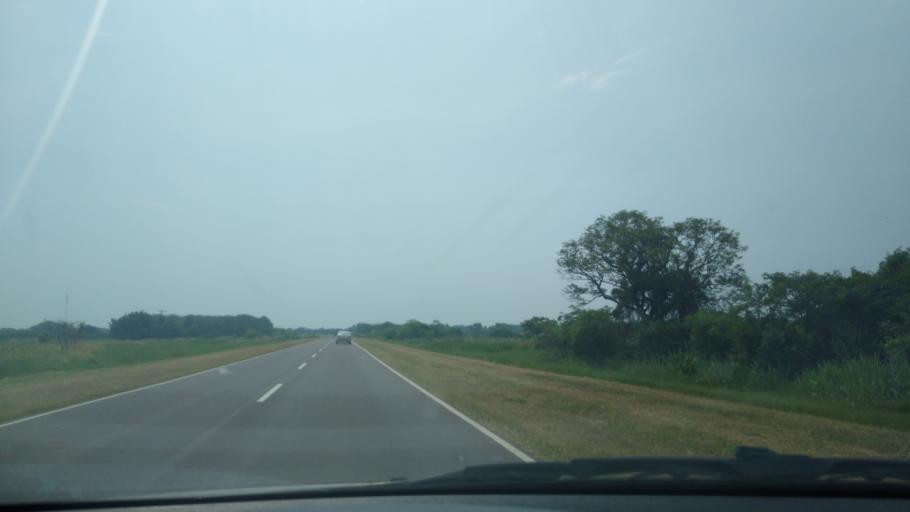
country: AR
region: Chaco
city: La Eduvigis
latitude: -26.8466
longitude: -59.0506
